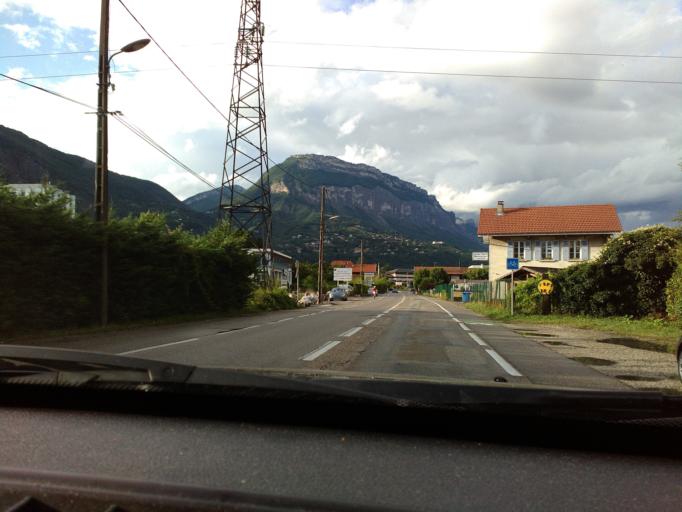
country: FR
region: Rhone-Alpes
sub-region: Departement de l'Isere
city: La Tronche
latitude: 45.1949
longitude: 5.7472
